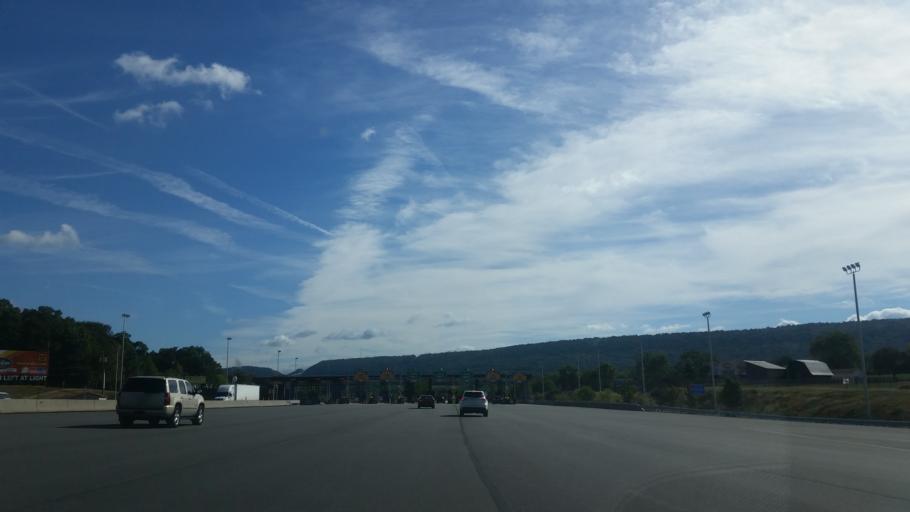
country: US
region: Pennsylvania
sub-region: Bedford County
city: Earlston
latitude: 39.9888
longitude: -78.2546
